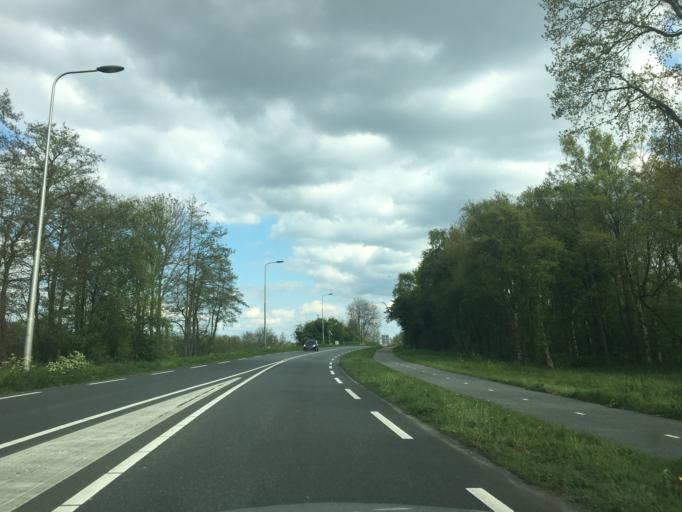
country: NL
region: Utrecht
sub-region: Stichtse Vecht
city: Vreeland
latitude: 52.2348
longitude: 5.0612
